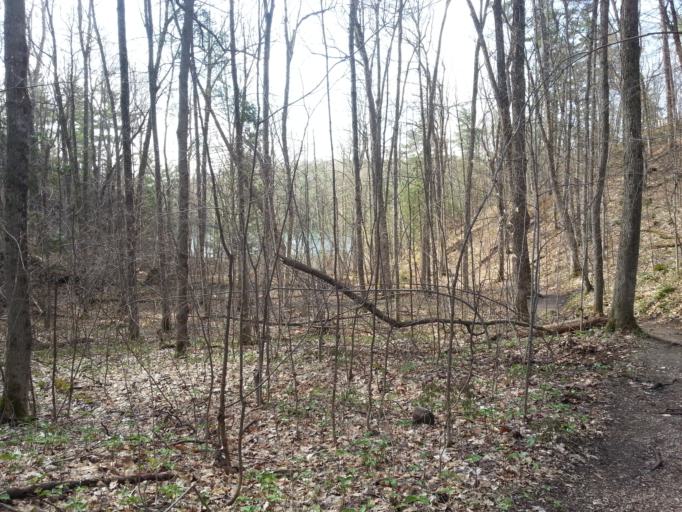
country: CA
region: Quebec
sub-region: Outaouais
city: Gatineau
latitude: 45.4702
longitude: -75.8073
